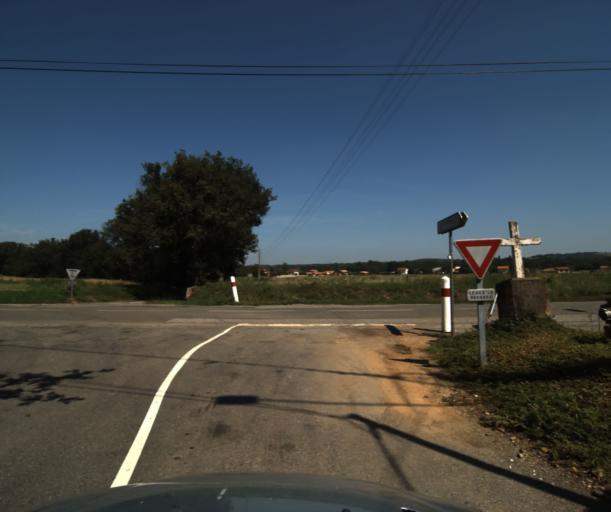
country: FR
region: Midi-Pyrenees
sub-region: Departement de la Haute-Garonne
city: Labastidette
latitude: 43.4485
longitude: 1.2924
